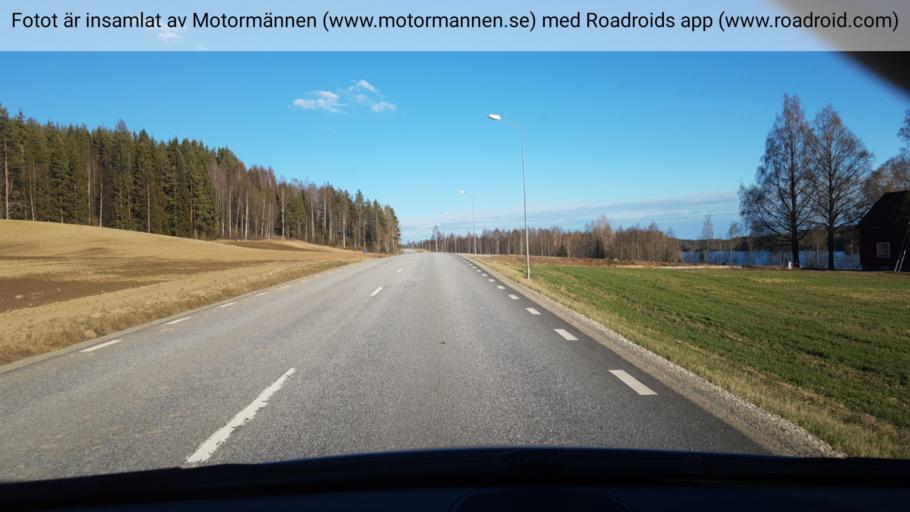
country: SE
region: Vaesterbotten
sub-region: Vindelns Kommun
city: Vindeln
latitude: 64.1357
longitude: 19.5276
